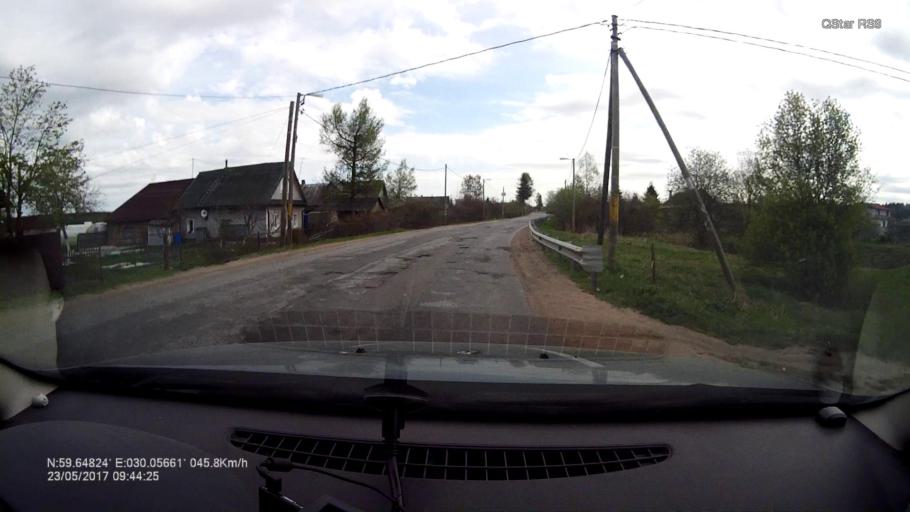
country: RU
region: Leningrad
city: Taytsy
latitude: 59.6482
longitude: 30.0567
